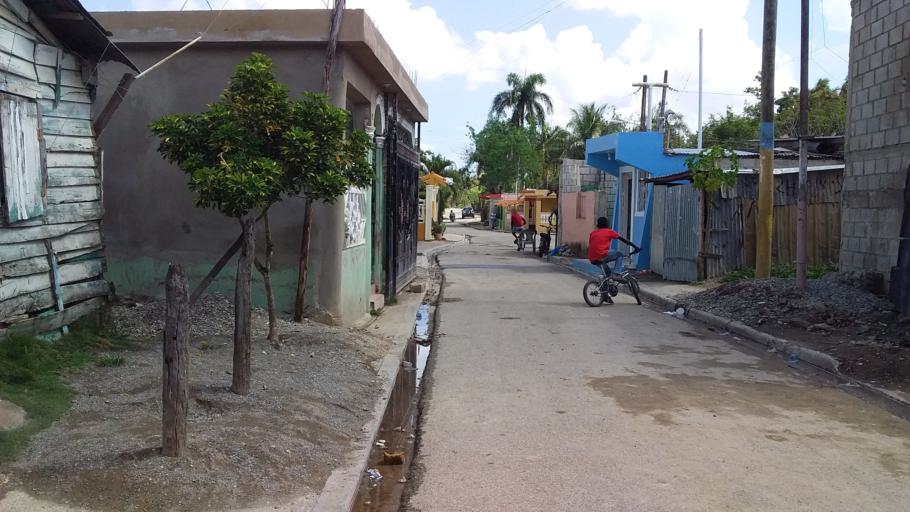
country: DO
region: Santo Domingo
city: Guerra
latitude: 18.5616
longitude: -69.7802
